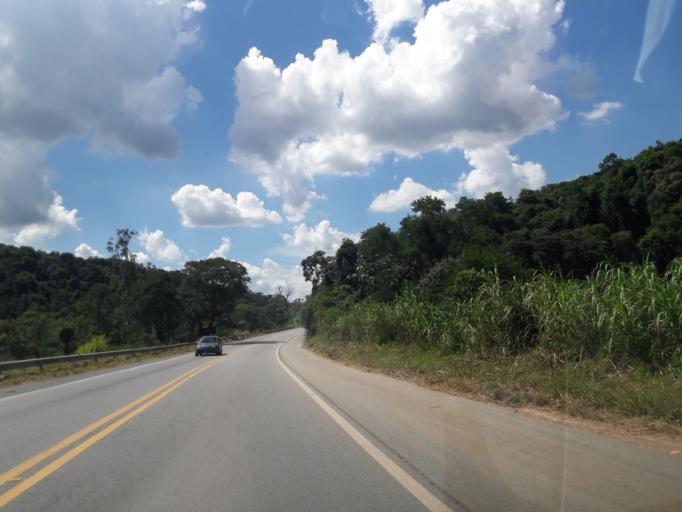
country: BR
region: Sao Paulo
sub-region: Campo Limpo Paulista
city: Campo Limpo Paulista
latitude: -23.2418
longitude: -46.7926
